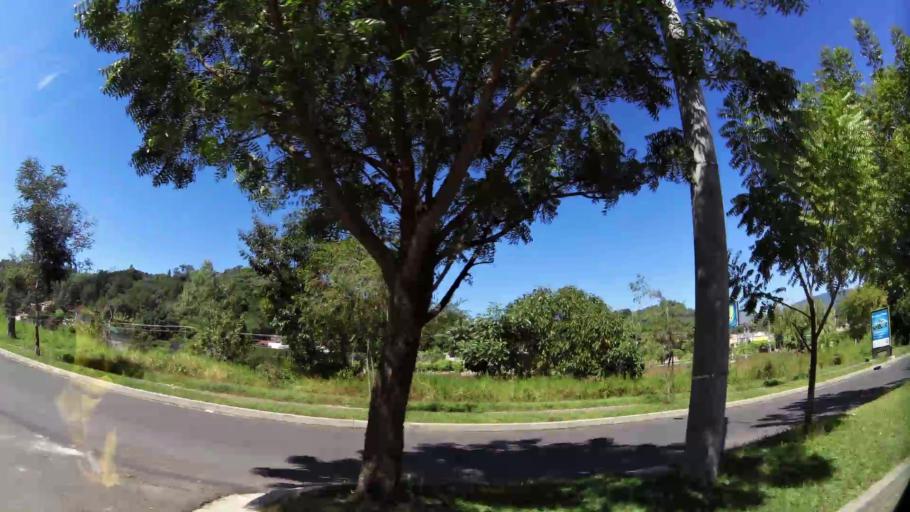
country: SV
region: La Libertad
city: Nuevo Cuscatlan
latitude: 13.6519
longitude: -89.2807
